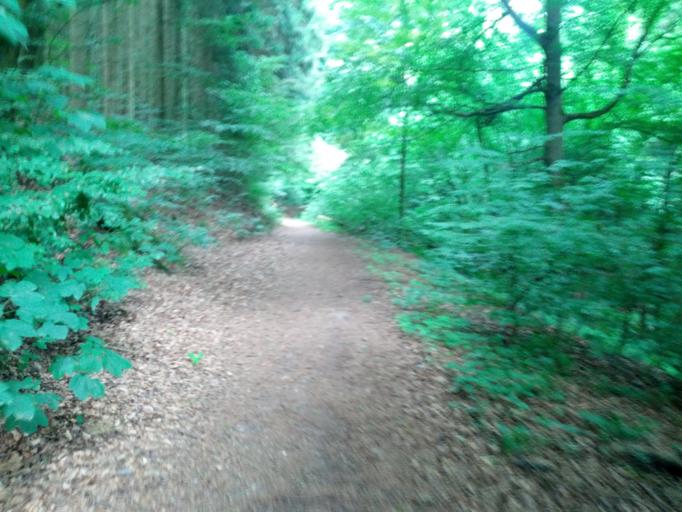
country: DE
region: Thuringia
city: Eisenach
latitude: 50.9592
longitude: 10.3245
